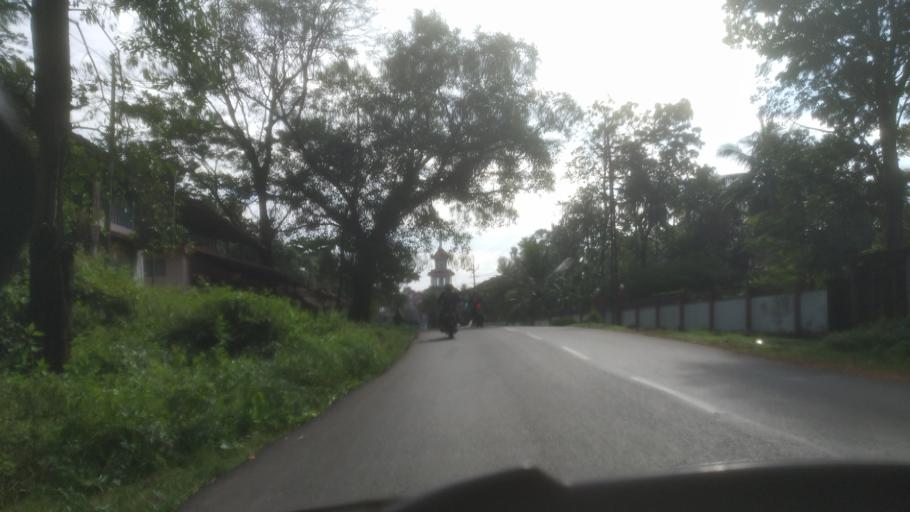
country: IN
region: Kerala
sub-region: Ernakulam
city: Kotamangalam
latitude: 10.0585
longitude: 76.6806
